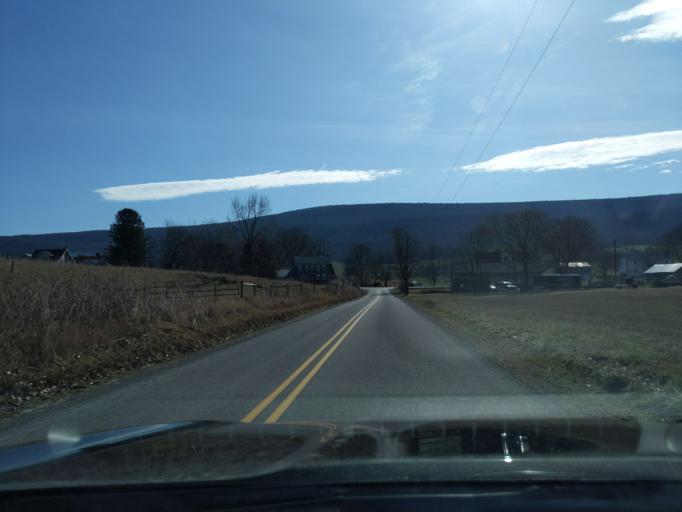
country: US
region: Pennsylvania
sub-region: Blair County
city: Williamsburg
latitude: 40.3745
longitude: -78.2383
